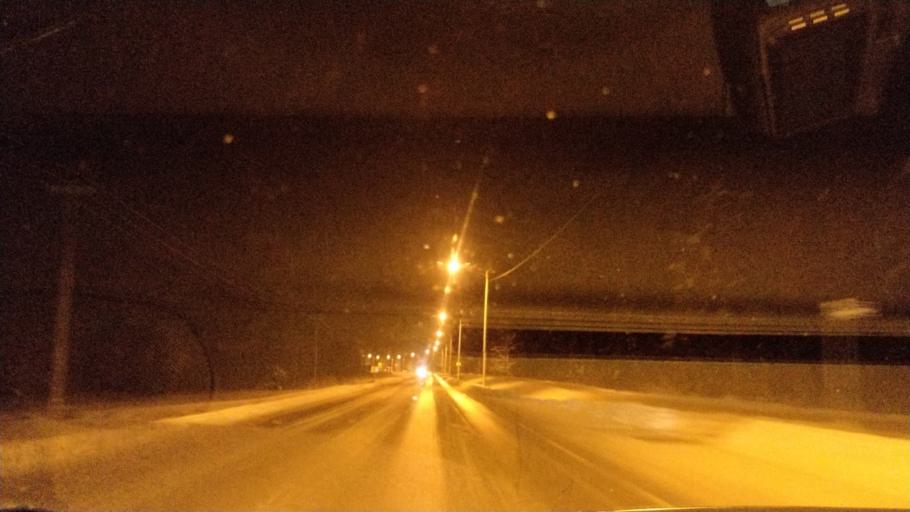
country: FI
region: Lapland
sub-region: Rovaniemi
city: Rovaniemi
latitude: 66.3045
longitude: 25.3567
